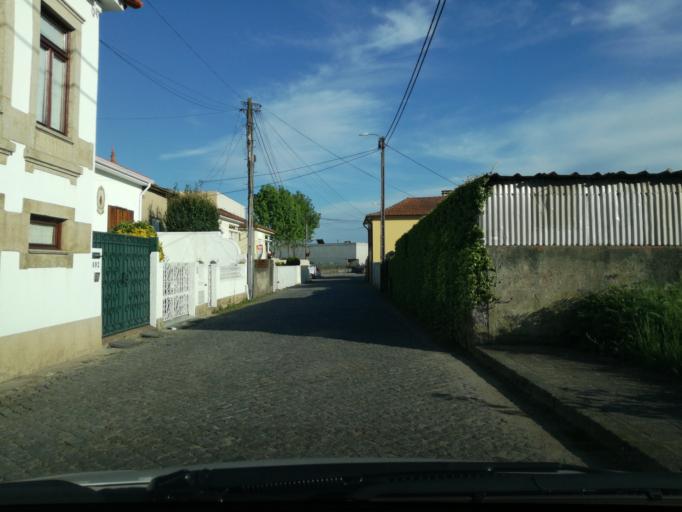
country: PT
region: Porto
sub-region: Maia
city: Gemunde
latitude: 41.2532
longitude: -8.6491
